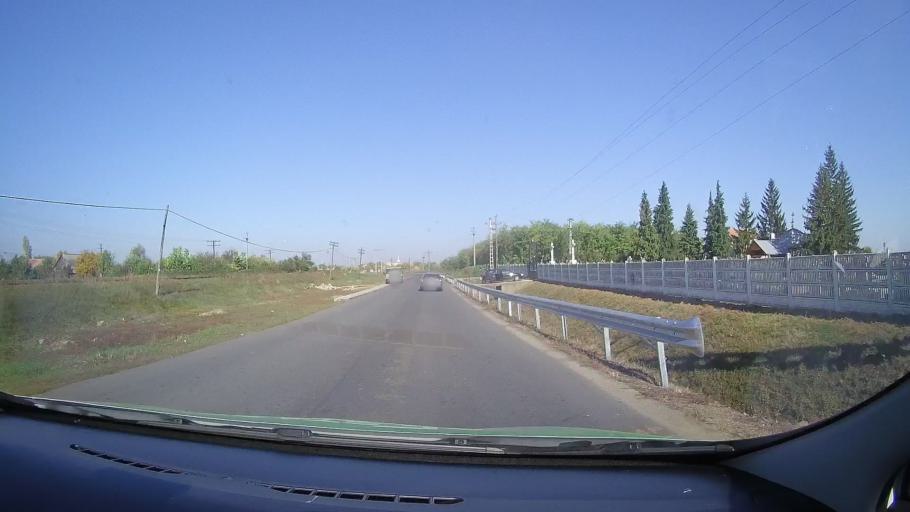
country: RO
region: Satu Mare
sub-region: Comuna Berveni
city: Lucaceni
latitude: 47.7454
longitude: 22.4743
